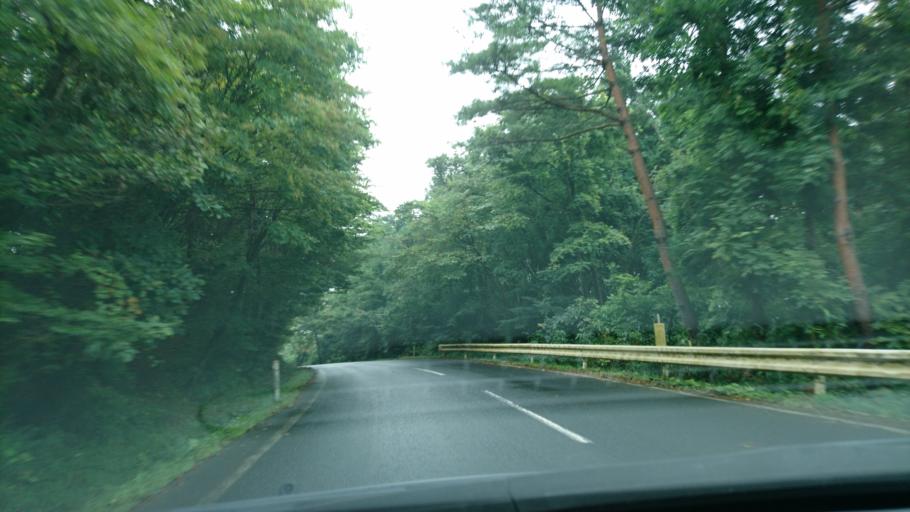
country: JP
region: Iwate
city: Ichinoseki
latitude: 38.9336
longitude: 141.1991
